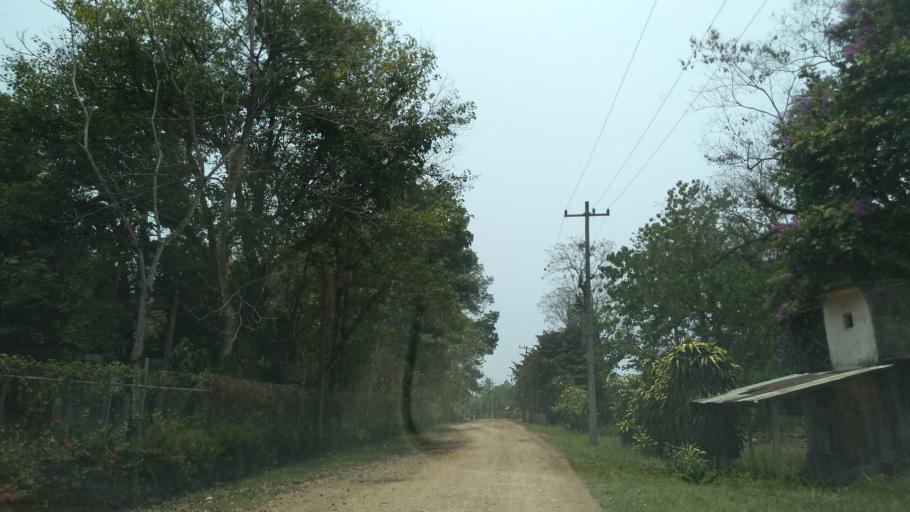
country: MX
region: Veracruz
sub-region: Tezonapa
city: Laguna Chica (Pueblo Nuevo)
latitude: 18.5159
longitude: -96.7628
